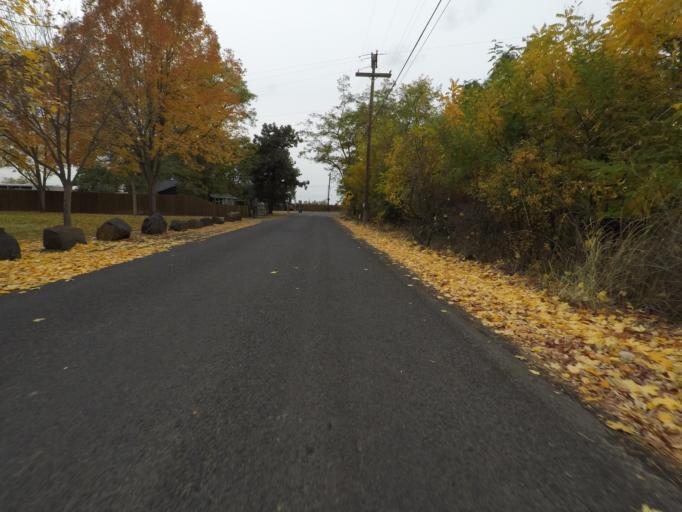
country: US
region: Washington
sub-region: Walla Walla County
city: Walla Walla East
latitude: 46.0749
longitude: -118.2826
